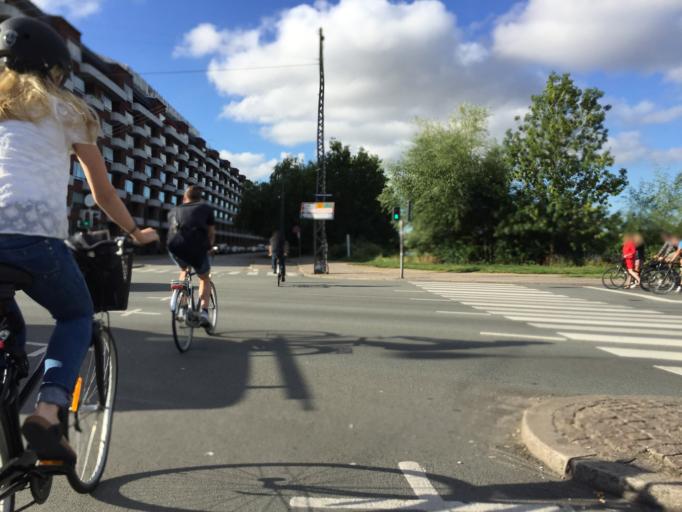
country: DK
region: Capital Region
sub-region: Kobenhavn
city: Copenhagen
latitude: 55.6811
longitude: 12.5603
